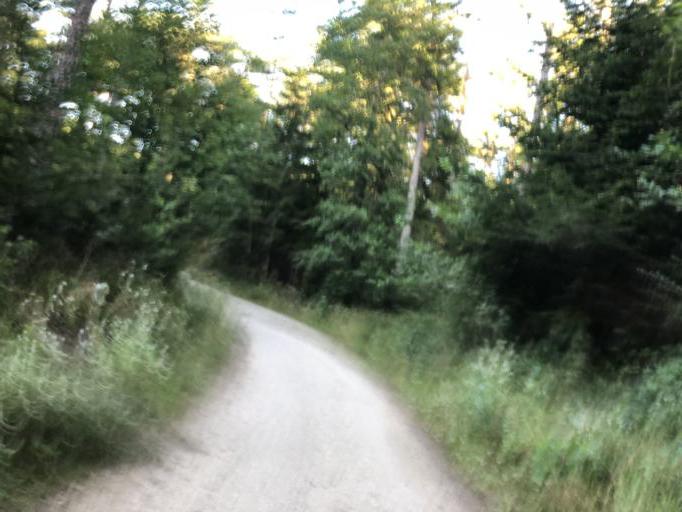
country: DE
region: Bavaria
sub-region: Regierungsbezirk Mittelfranken
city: Kalchreuth
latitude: 49.5511
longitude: 11.1047
